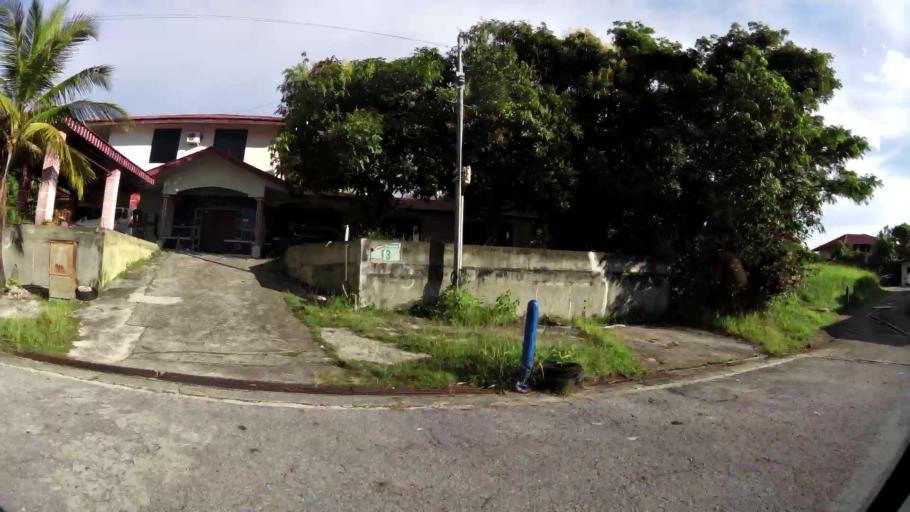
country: BN
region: Brunei and Muara
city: Bandar Seri Begawan
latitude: 4.9806
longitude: 114.9693
